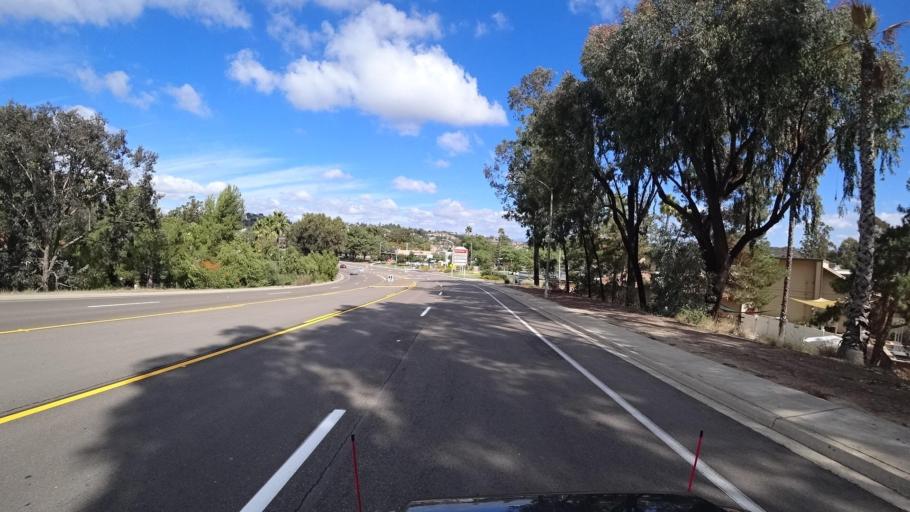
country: US
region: California
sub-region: San Diego County
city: Casa de Oro-Mount Helix
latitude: 32.7463
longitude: -116.9631
